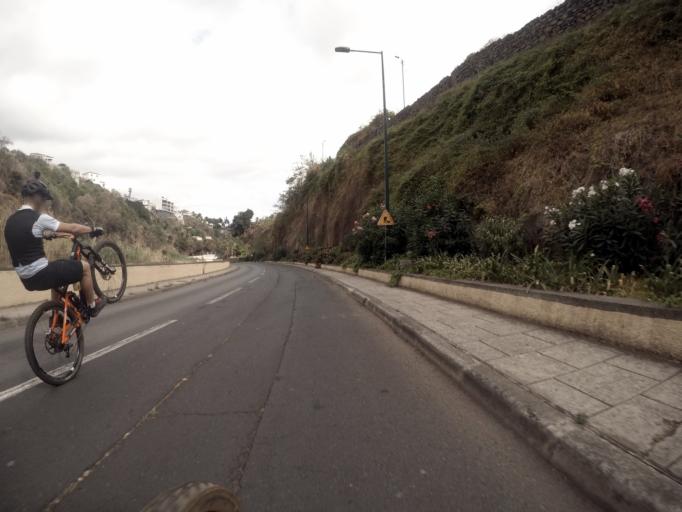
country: PT
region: Madeira
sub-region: Funchal
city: Nossa Senhora do Monte
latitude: 32.6576
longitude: -16.9246
